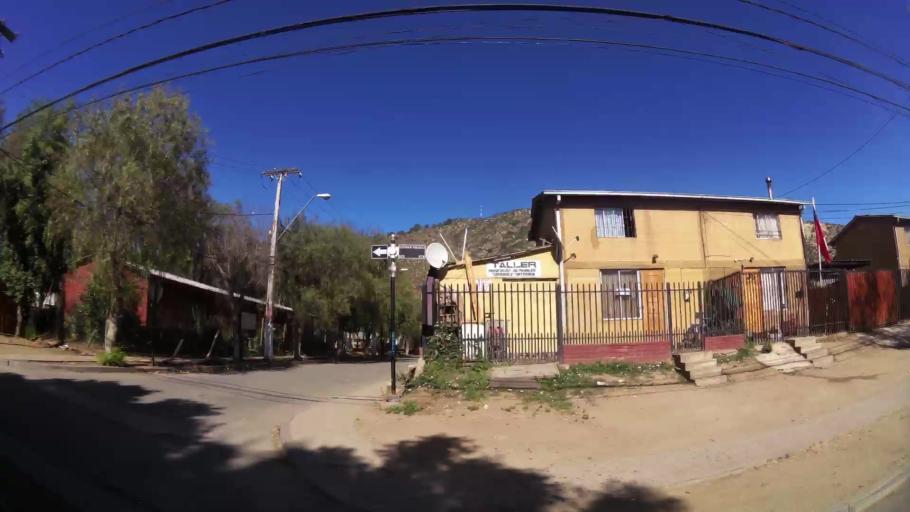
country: CL
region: Santiago Metropolitan
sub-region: Provincia de Chacabuco
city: Lampa
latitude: -33.3966
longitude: -71.1297
